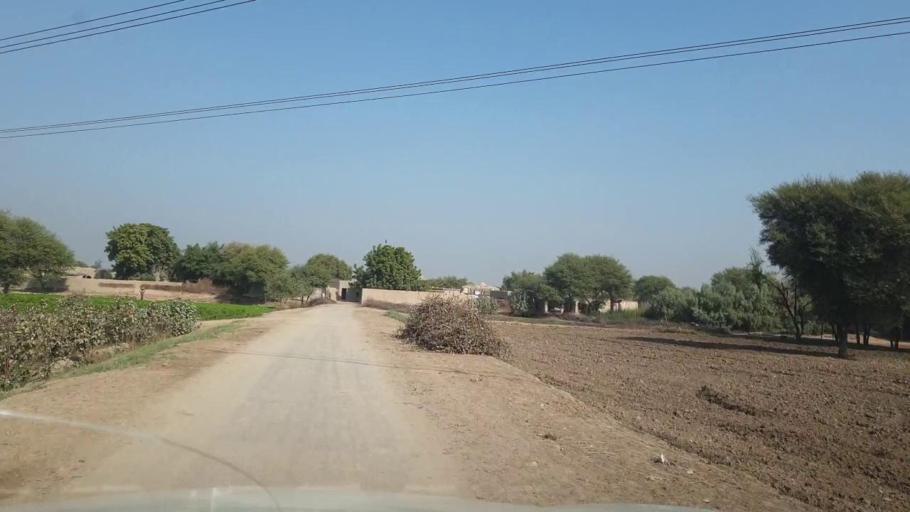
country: PK
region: Sindh
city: Bhan
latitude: 26.5409
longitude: 67.7639
